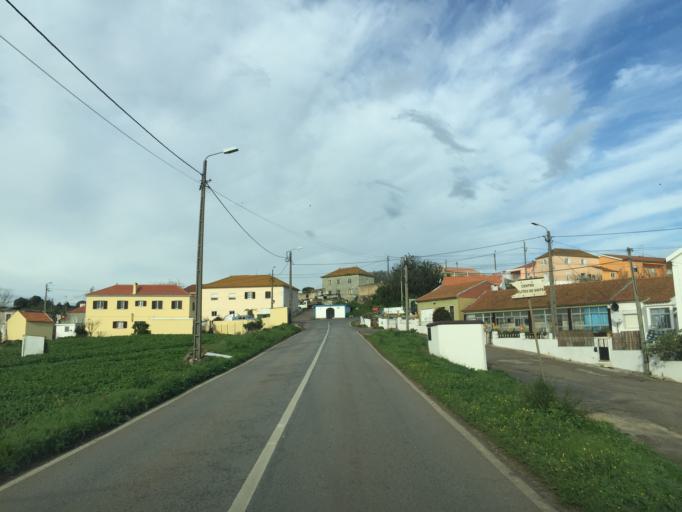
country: PT
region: Lisbon
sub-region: Sintra
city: Almargem
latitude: 38.8670
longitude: -9.2841
